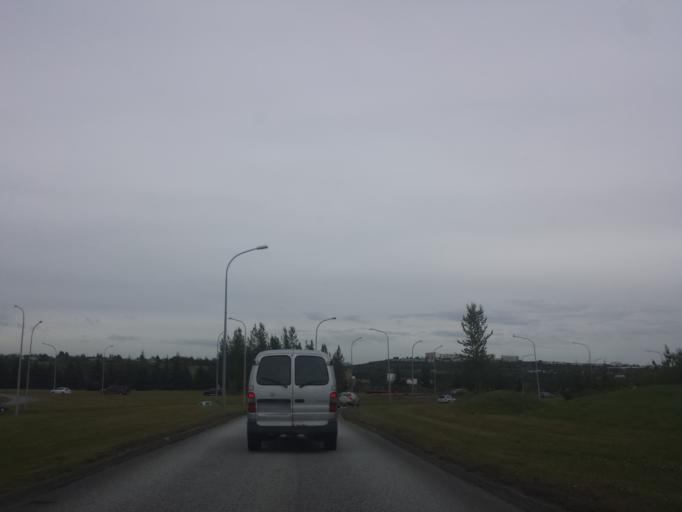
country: IS
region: Capital Region
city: Reykjavik
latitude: 64.1233
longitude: -21.8496
